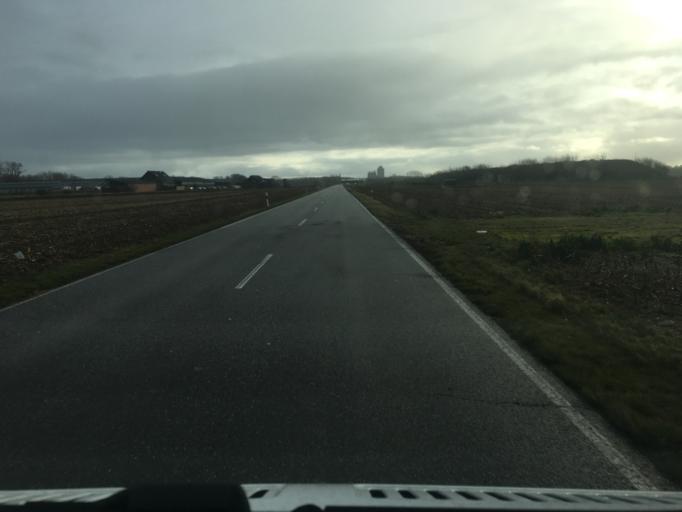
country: DE
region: North Rhine-Westphalia
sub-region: Regierungsbezirk Koln
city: Inden
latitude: 50.8600
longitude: 6.4173
